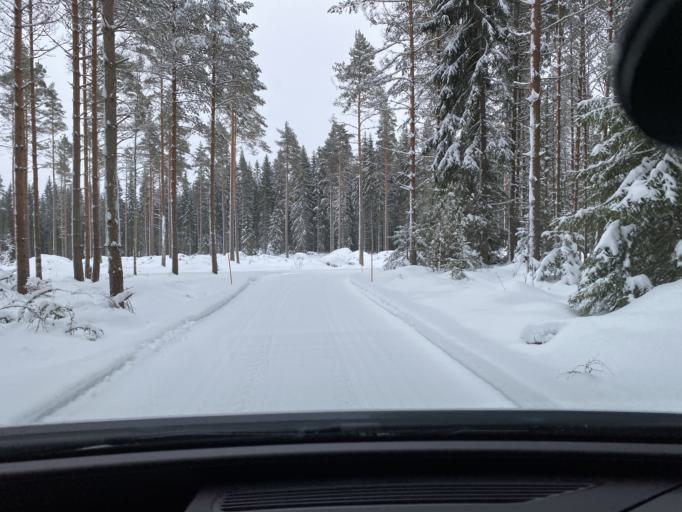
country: FI
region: Pirkanmaa
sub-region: Lounais-Pirkanmaa
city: Punkalaidun
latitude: 61.1340
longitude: 23.0964
